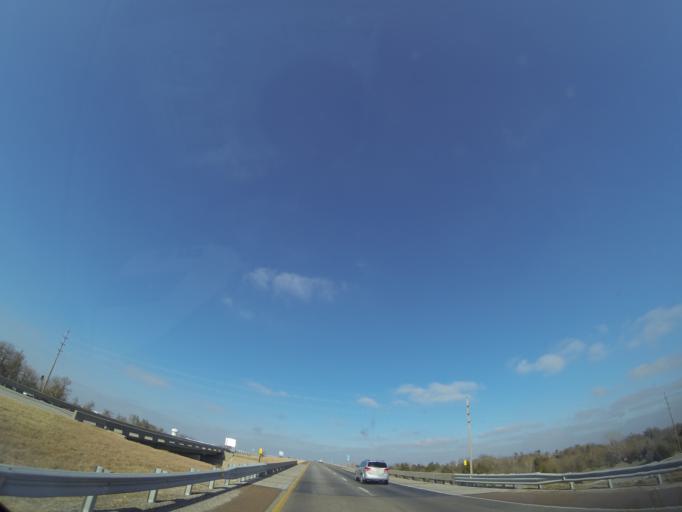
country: US
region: Kansas
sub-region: McPherson County
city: McPherson
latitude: 38.3766
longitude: -97.6205
